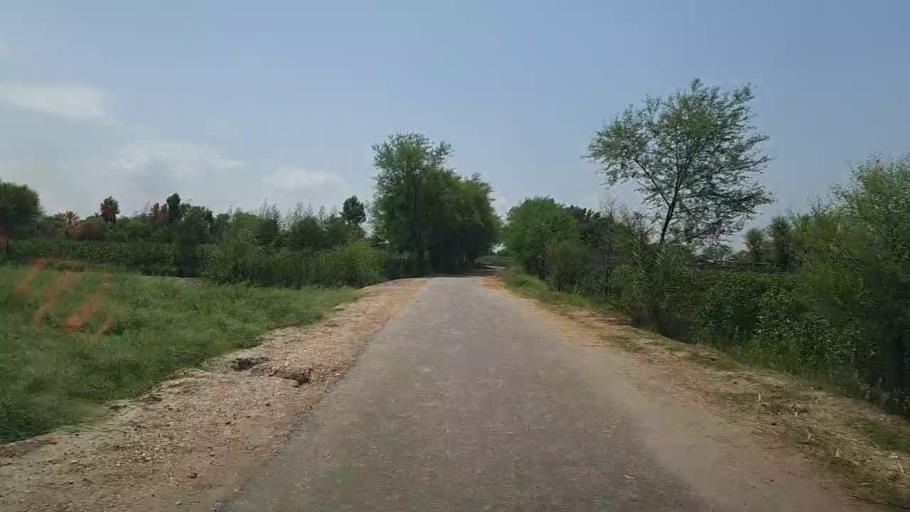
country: PK
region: Sindh
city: Ubauro
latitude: 28.1522
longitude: 69.7689
